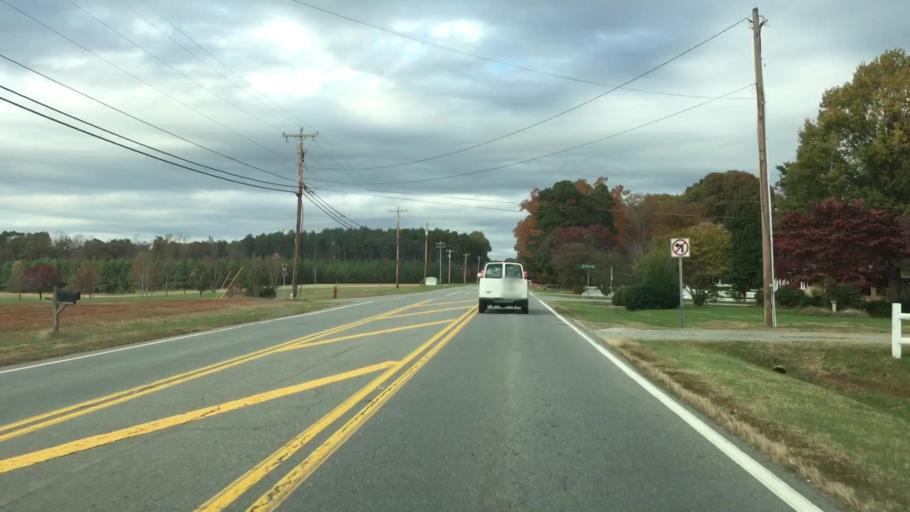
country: US
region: North Carolina
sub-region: Rockingham County
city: Reidsville
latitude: 36.3181
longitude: -79.7147
